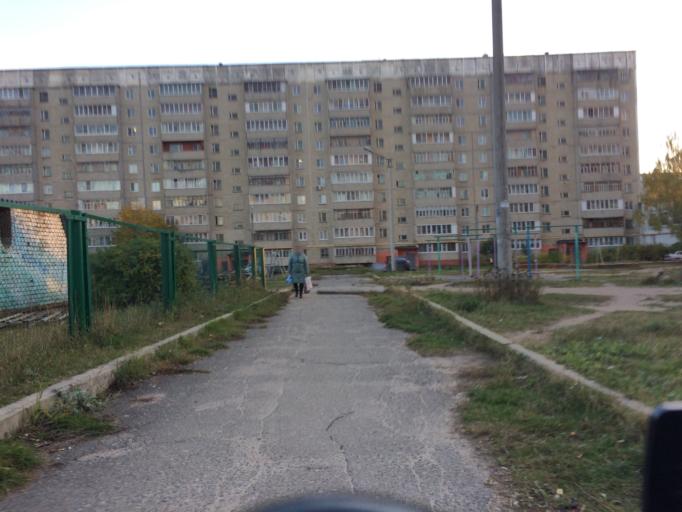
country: RU
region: Mariy-El
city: Yoshkar-Ola
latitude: 56.6356
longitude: 47.9286
